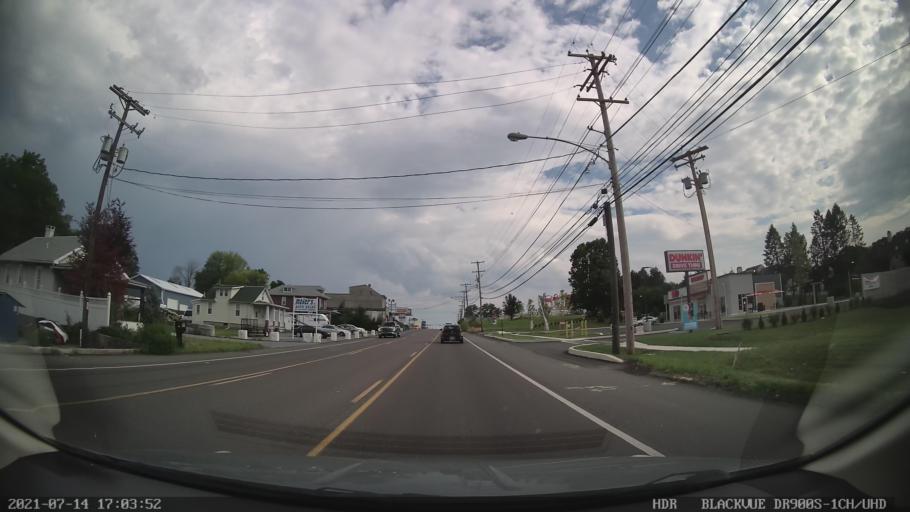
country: US
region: Pennsylvania
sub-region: Berks County
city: Muhlenberg Park
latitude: 40.3885
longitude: -75.9349
